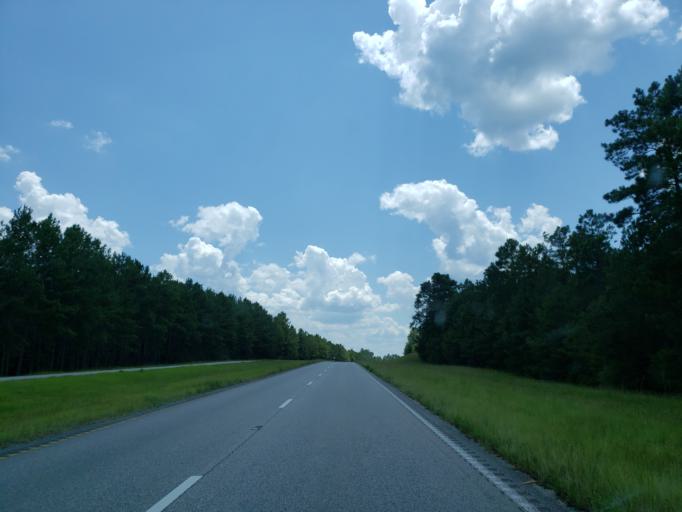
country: US
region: Mississippi
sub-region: Wayne County
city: Belmont
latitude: 31.3740
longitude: -88.4851
